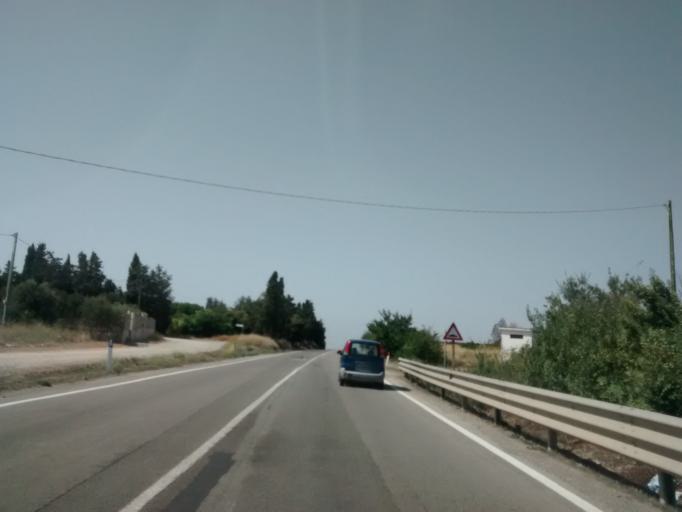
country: IT
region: Sardinia
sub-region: Provincia di Cagliari
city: Maracalagonis
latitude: 39.2611
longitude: 9.2308
